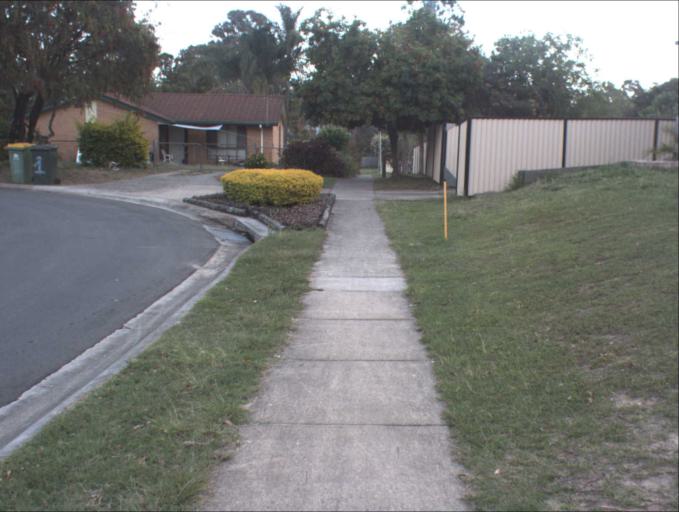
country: AU
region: Queensland
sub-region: Logan
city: Waterford West
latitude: -27.6822
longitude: 153.1318
